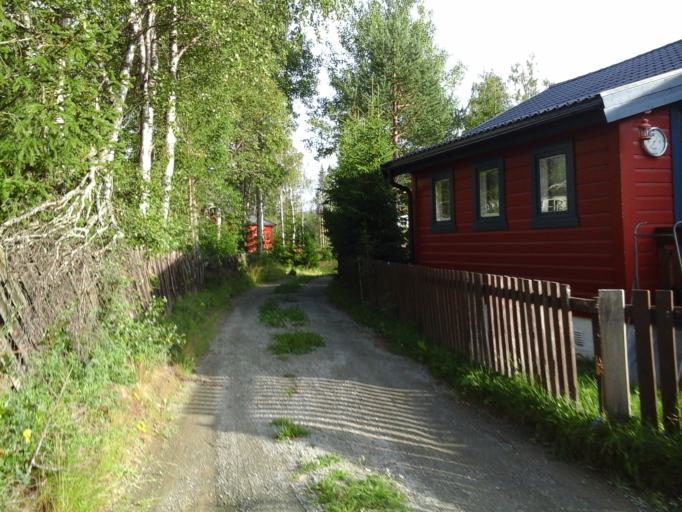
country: NO
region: Buskerud
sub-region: Hemsedal
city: Troim
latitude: 60.8444
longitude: 8.6188
